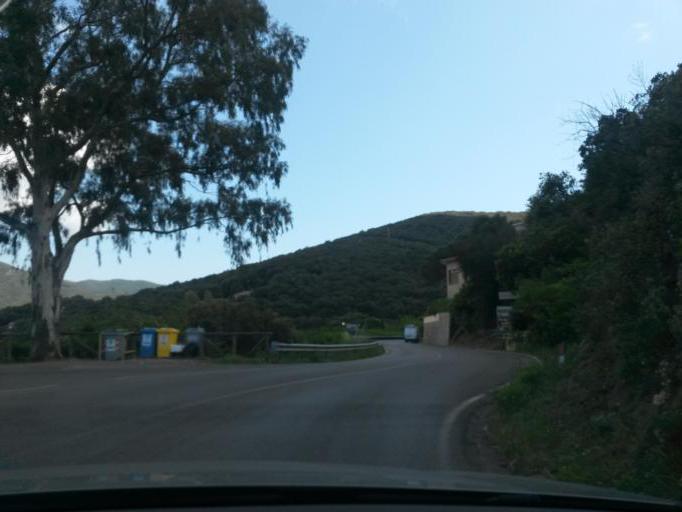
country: IT
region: Tuscany
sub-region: Provincia di Livorno
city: Marciana Marina
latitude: 42.7899
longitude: 10.2265
